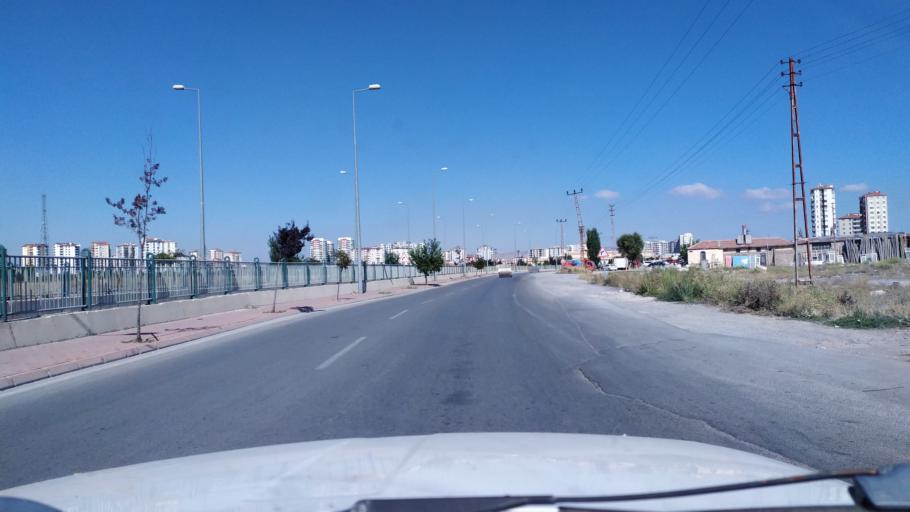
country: TR
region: Kayseri
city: Talas
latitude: 38.7342
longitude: 35.5476
